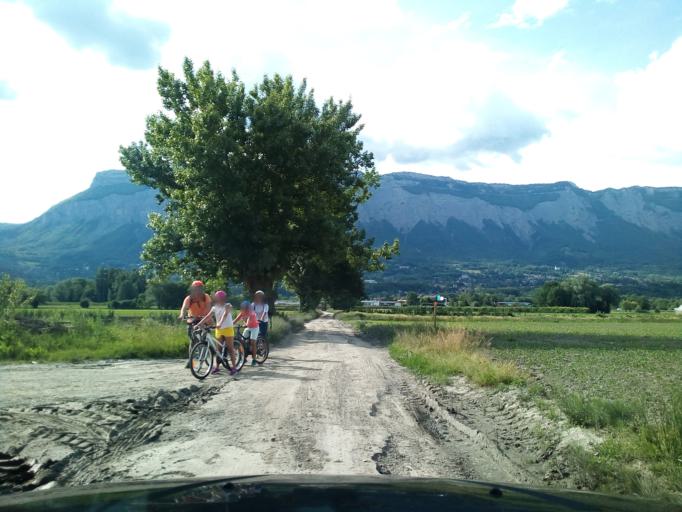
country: FR
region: Rhone-Alpes
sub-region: Departement de l'Isere
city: Montbonnot-Saint-Martin
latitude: 45.2136
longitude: 5.8192
